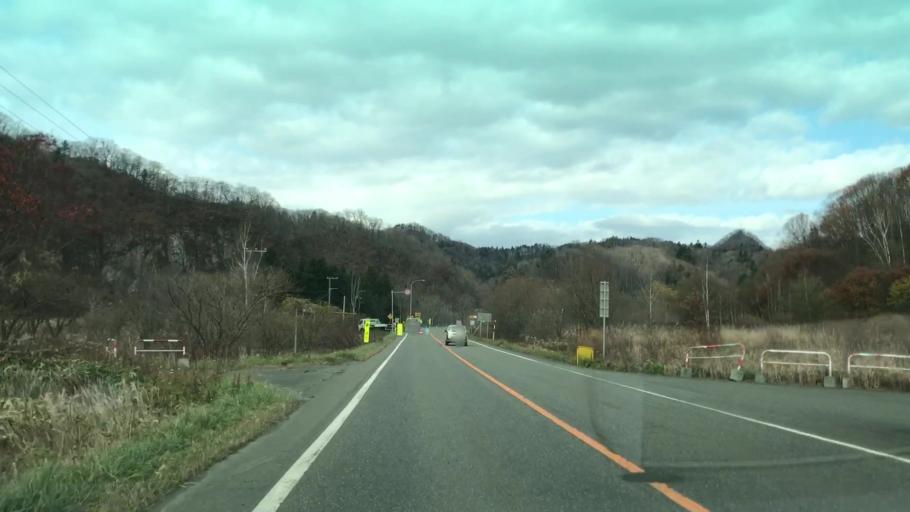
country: JP
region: Hokkaido
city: Shizunai-furukawacho
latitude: 42.7917
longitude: 142.3940
